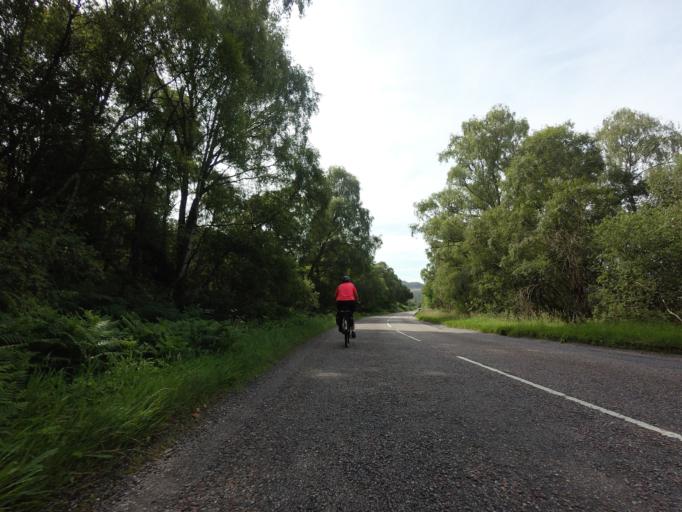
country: GB
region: Scotland
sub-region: Highland
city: Alness
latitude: 57.8501
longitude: -4.2675
